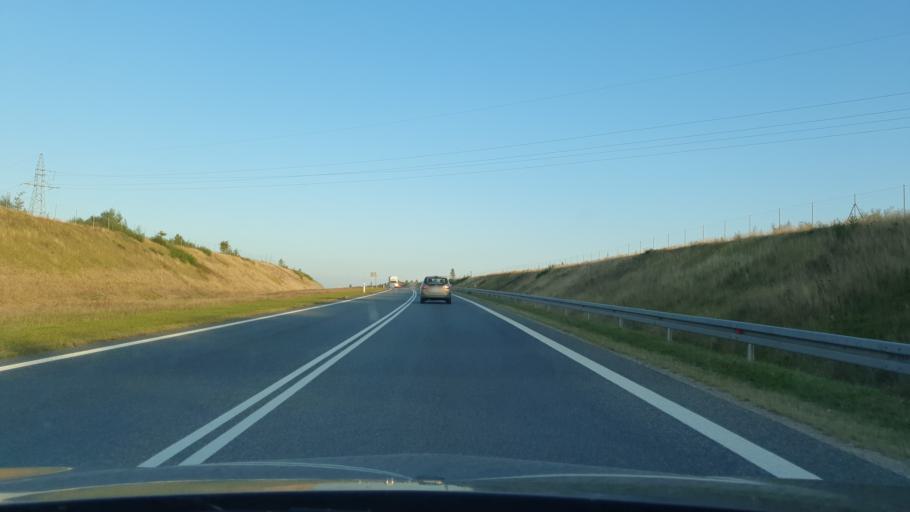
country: PL
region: Pomeranian Voivodeship
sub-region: Powiat slupski
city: Kobylnica
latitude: 54.4274
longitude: 16.9833
